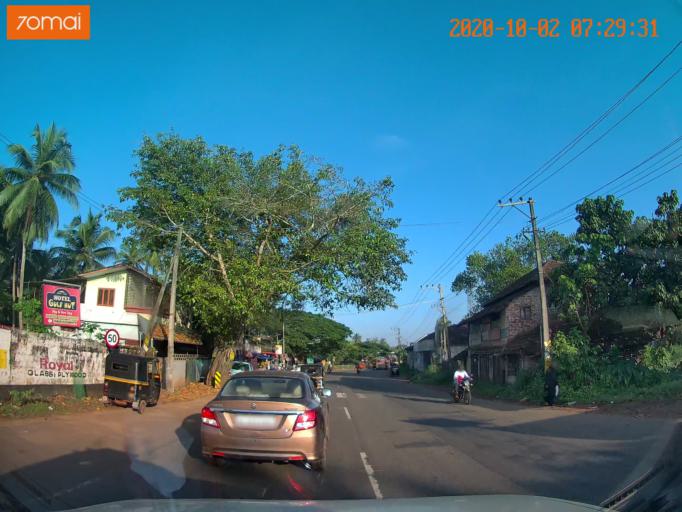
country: IN
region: Kerala
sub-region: Malappuram
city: Pariyapuram
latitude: 11.0347
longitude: 75.9386
